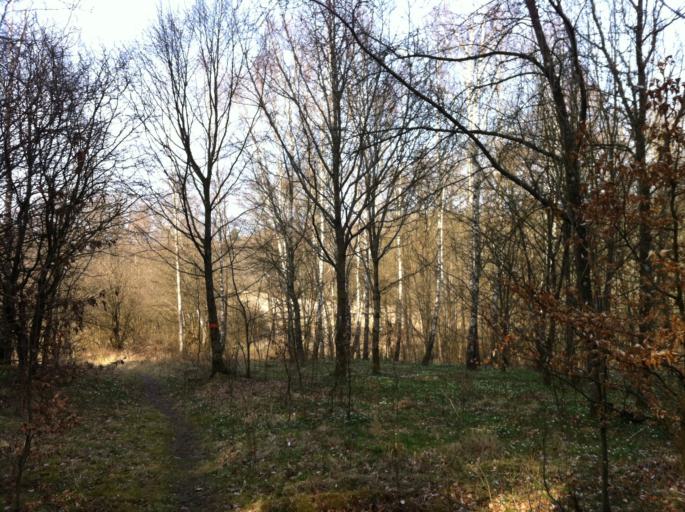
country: SE
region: Skane
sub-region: Eslovs Kommun
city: Stehag
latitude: 56.0123
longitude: 13.3876
